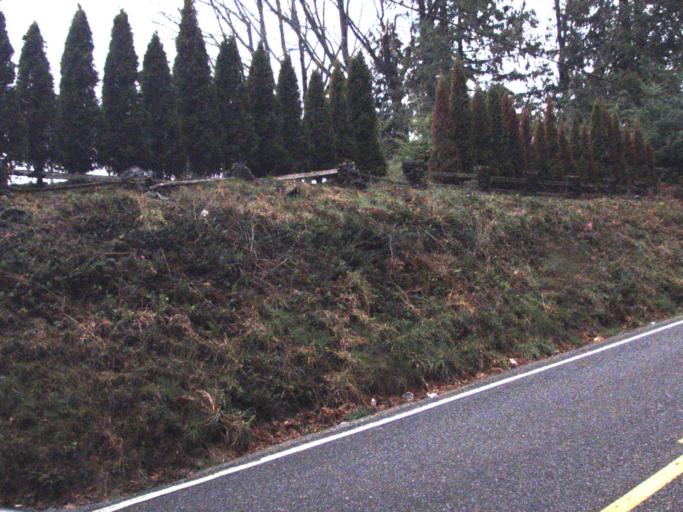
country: US
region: Washington
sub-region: Snohomish County
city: Warm Beach
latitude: 48.1531
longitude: -122.2879
